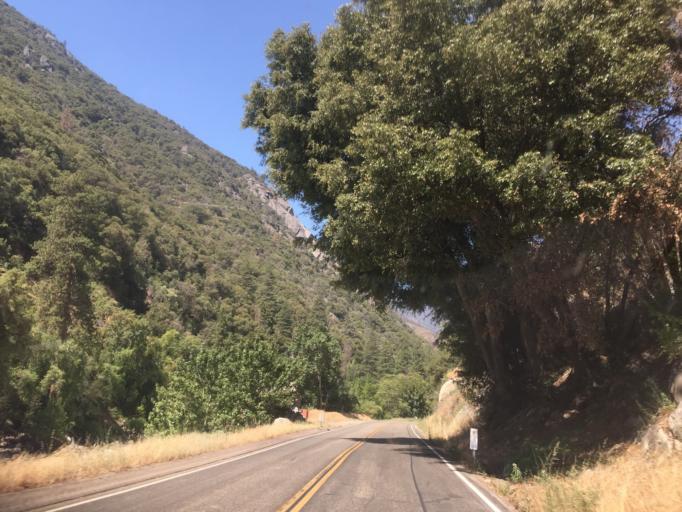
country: US
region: California
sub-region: Tulare County
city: Three Rivers
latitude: 36.8089
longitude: -118.7675
